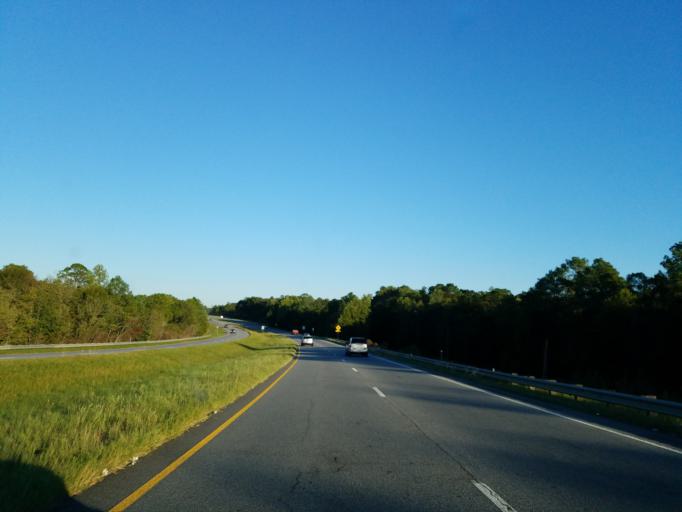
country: US
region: Georgia
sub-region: Worth County
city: Sylvester
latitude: 31.5114
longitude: -83.7751
